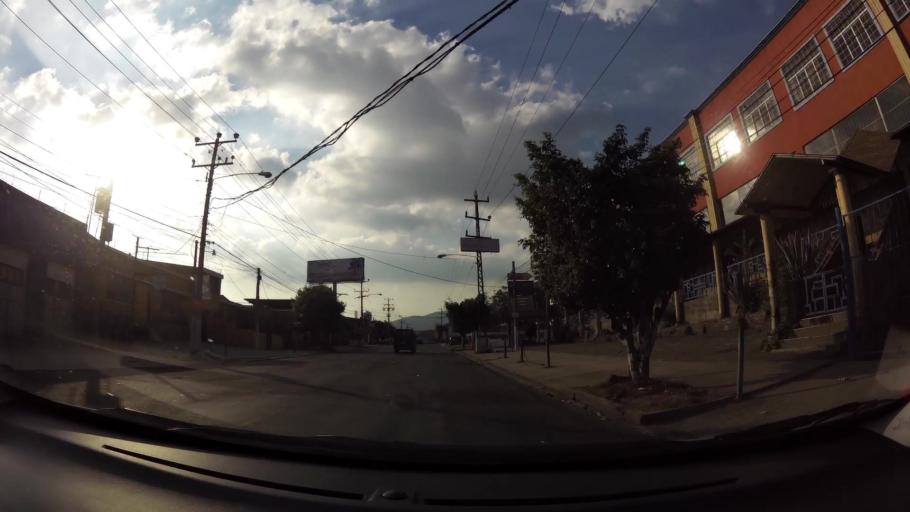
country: SV
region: San Salvador
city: San Salvador
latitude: 13.6933
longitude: -89.2212
